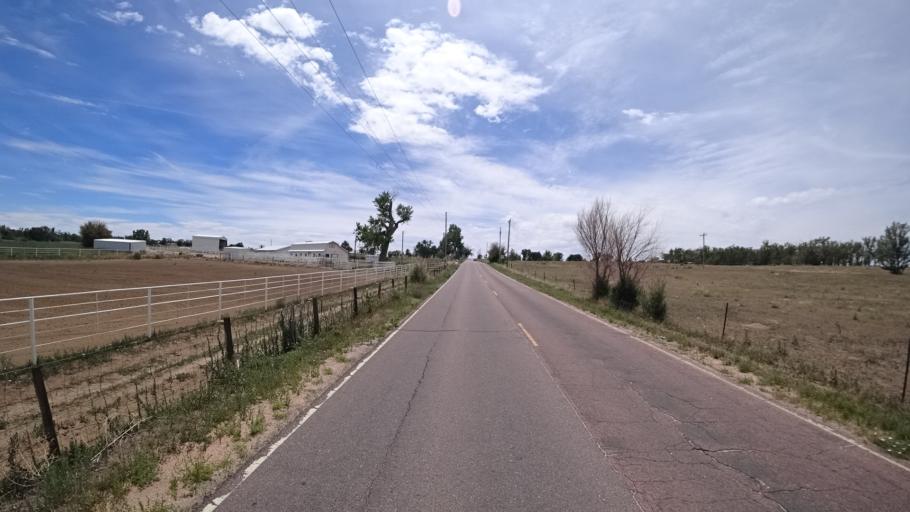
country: US
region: Colorado
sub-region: El Paso County
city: Fountain
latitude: 38.6853
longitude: -104.6735
